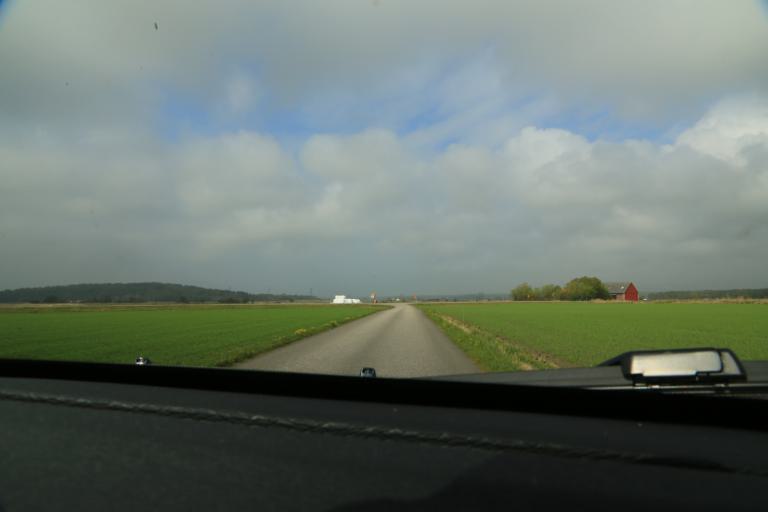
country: SE
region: Halland
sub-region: Kungsbacka Kommun
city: Frillesas
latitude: 57.2354
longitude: 12.1588
